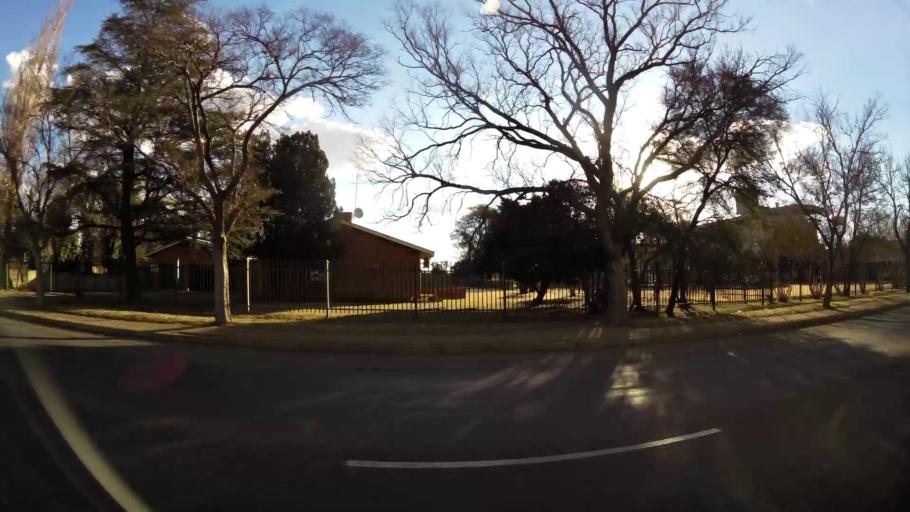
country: ZA
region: North-West
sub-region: Dr Kenneth Kaunda District Municipality
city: Potchefstroom
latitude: -26.7315
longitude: 27.0841
